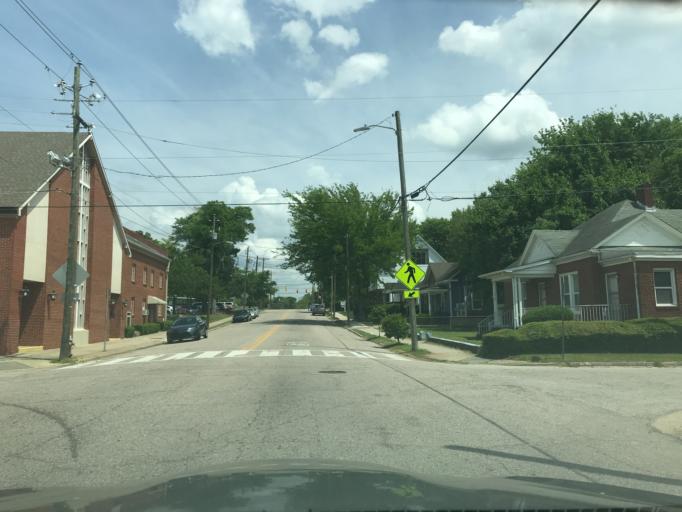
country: US
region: North Carolina
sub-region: Wake County
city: Raleigh
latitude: 35.7764
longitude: -78.6242
